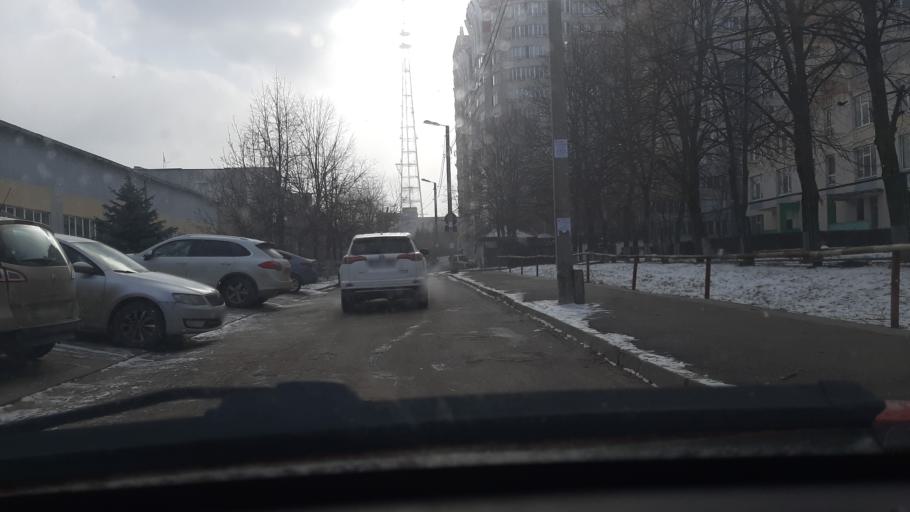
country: MD
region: Chisinau
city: Chisinau
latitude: 47.0040
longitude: 28.8059
